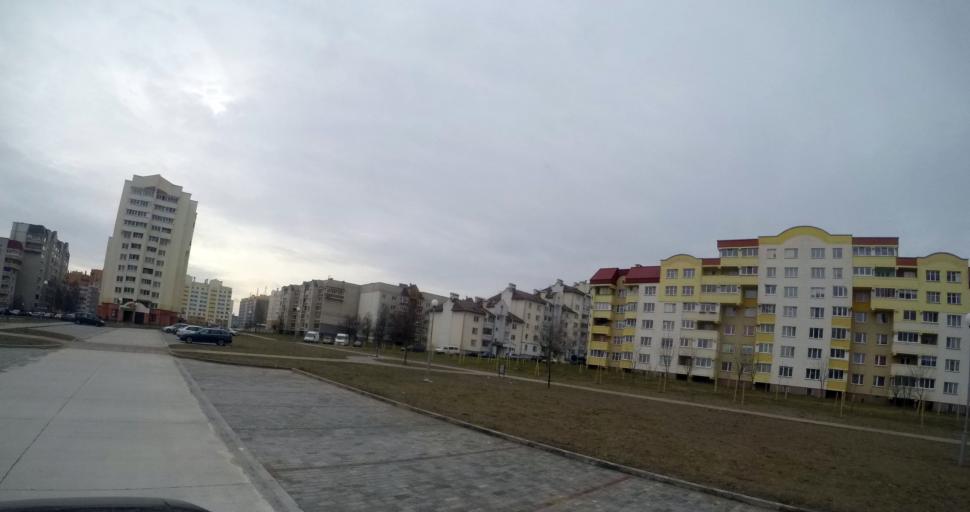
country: BY
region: Grodnenskaya
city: Hrodna
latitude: 53.7135
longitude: 23.8534
